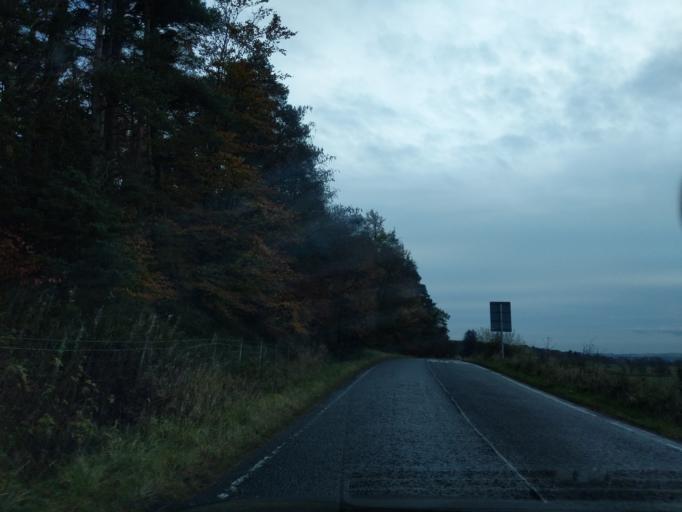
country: GB
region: Scotland
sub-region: West Lothian
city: Linlithgow
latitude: 55.9441
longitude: -3.6172
